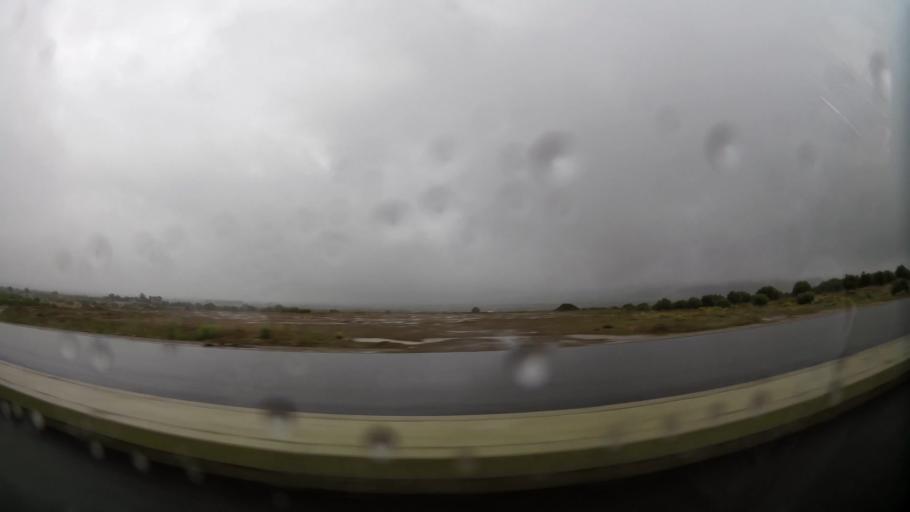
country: MA
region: Oriental
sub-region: Nador
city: Midar
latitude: 34.8623
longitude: -3.7233
